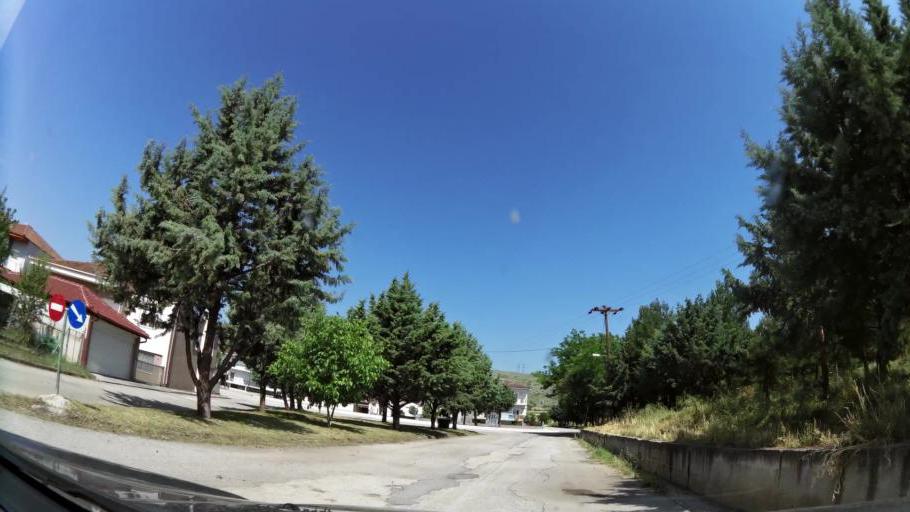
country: GR
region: West Macedonia
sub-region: Nomos Kozanis
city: Koila
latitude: 40.3381
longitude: 21.7883
